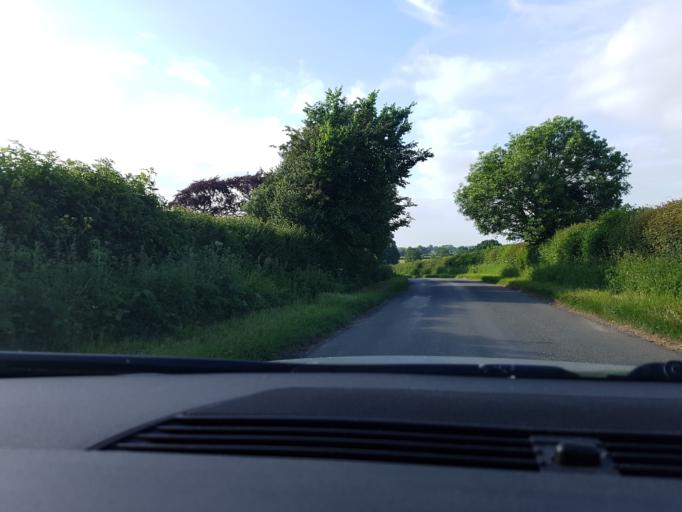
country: GB
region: England
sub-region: Northamptonshire
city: Deanshanger
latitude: 52.0377
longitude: -0.9107
